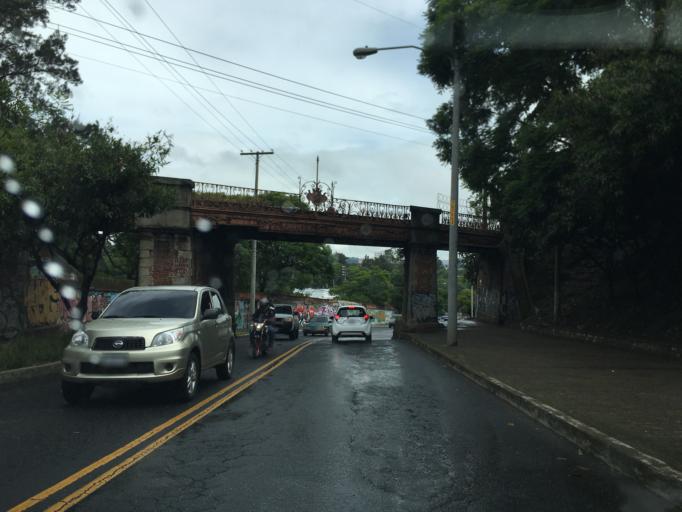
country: GT
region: Guatemala
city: Guatemala City
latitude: 14.6271
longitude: -90.5111
